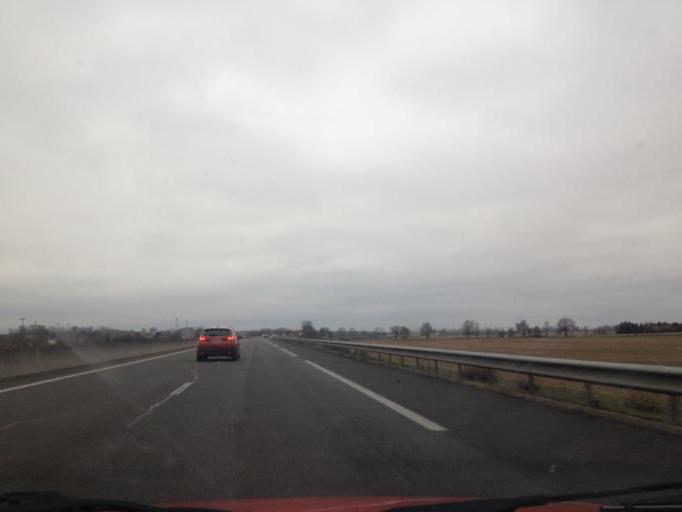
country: FR
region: Auvergne
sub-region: Departement de l'Allier
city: Toulon-sur-Allier
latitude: 46.5177
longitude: 3.3534
